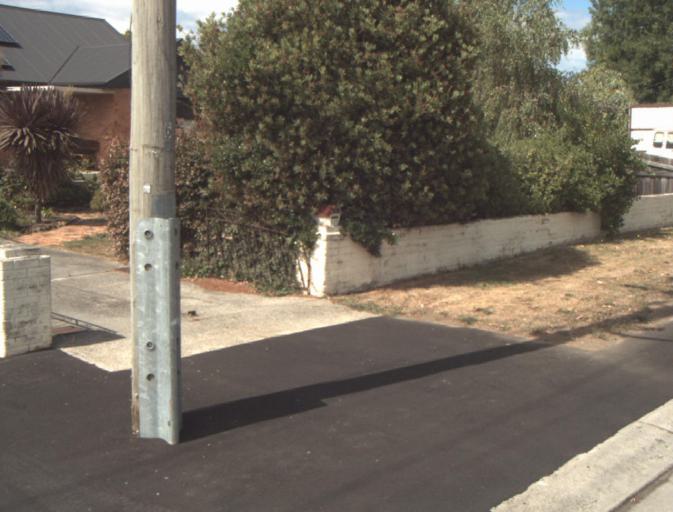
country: AU
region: Tasmania
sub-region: Launceston
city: Summerhill
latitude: -41.4639
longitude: 147.1366
